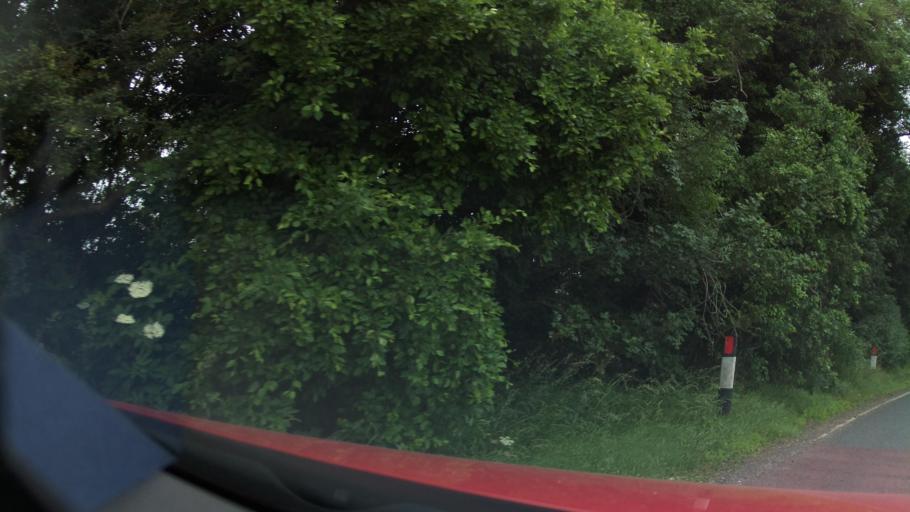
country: GB
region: England
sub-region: District of Rutland
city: Exton
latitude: 52.6678
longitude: -0.6291
